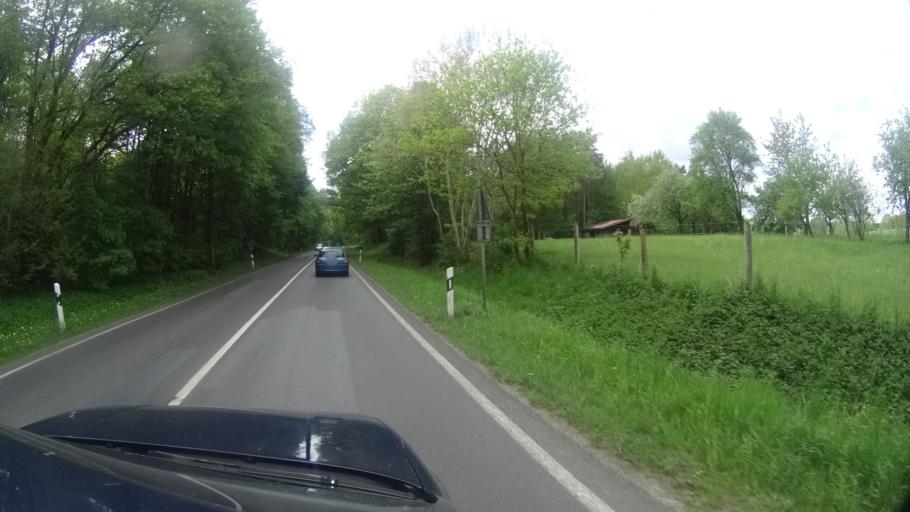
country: DE
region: Mecklenburg-Vorpommern
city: Malchow
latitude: 53.4857
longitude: 12.3984
